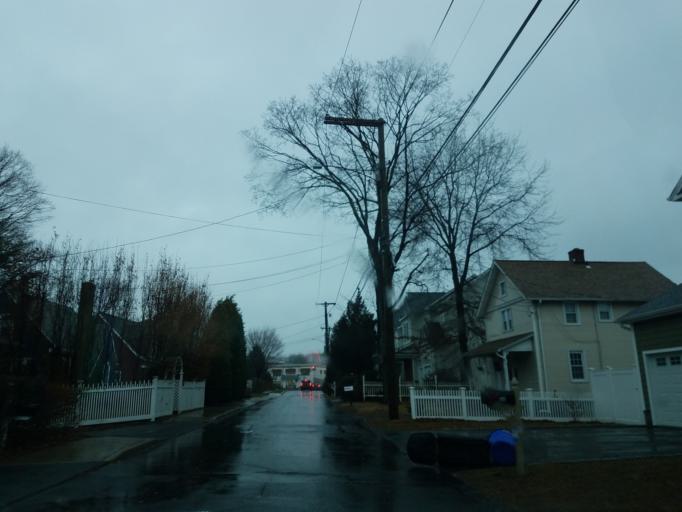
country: US
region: Connecticut
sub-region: Fairfield County
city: Southport
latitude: 41.1374
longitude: -73.2922
